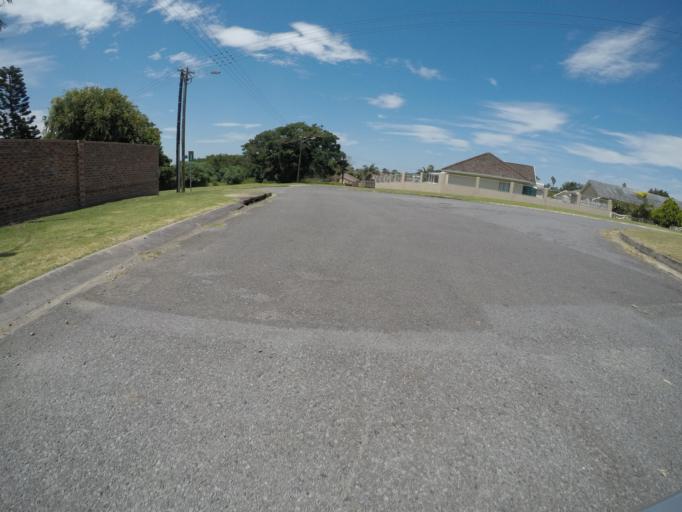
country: ZA
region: Eastern Cape
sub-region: Buffalo City Metropolitan Municipality
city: East London
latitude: -33.0311
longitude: 27.8661
